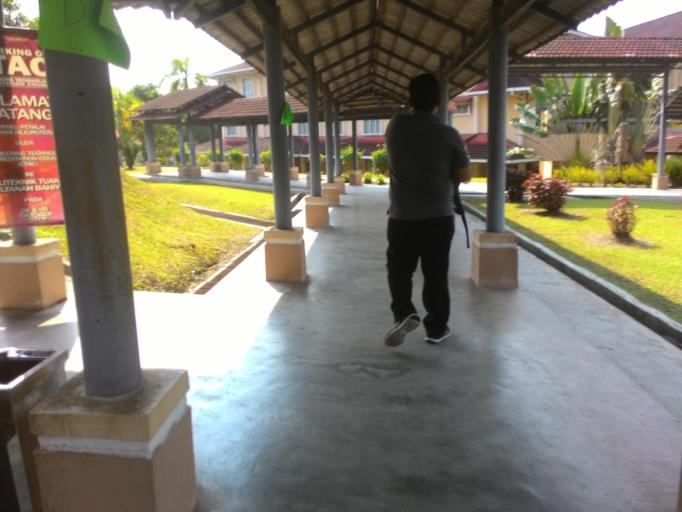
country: MY
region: Kedah
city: Kulim
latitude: 5.3842
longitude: 100.5784
